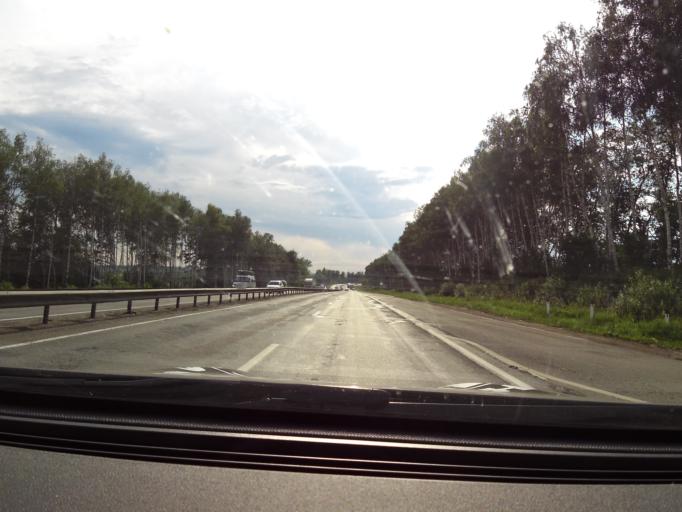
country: RU
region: Vladimir
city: Gorokhovets
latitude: 56.1592
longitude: 42.5290
